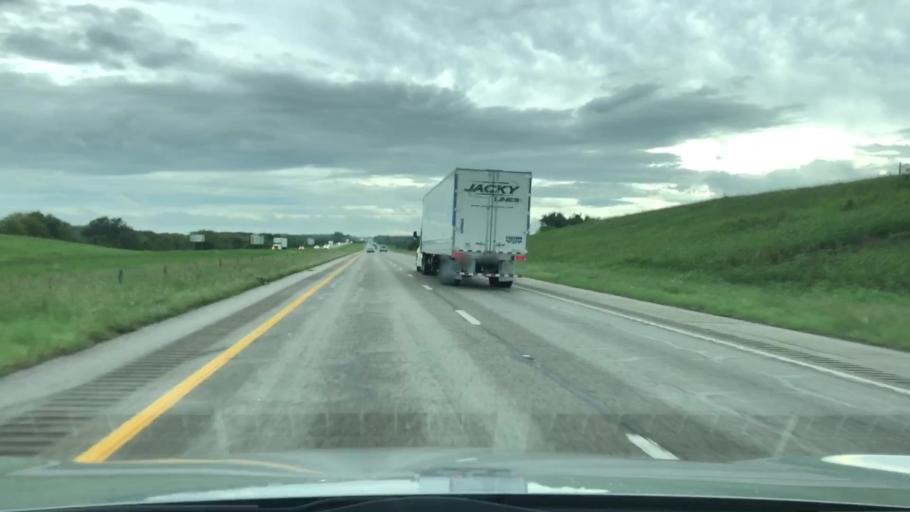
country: US
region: Texas
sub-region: Caldwell County
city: Luling
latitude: 29.6505
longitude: -97.6525
